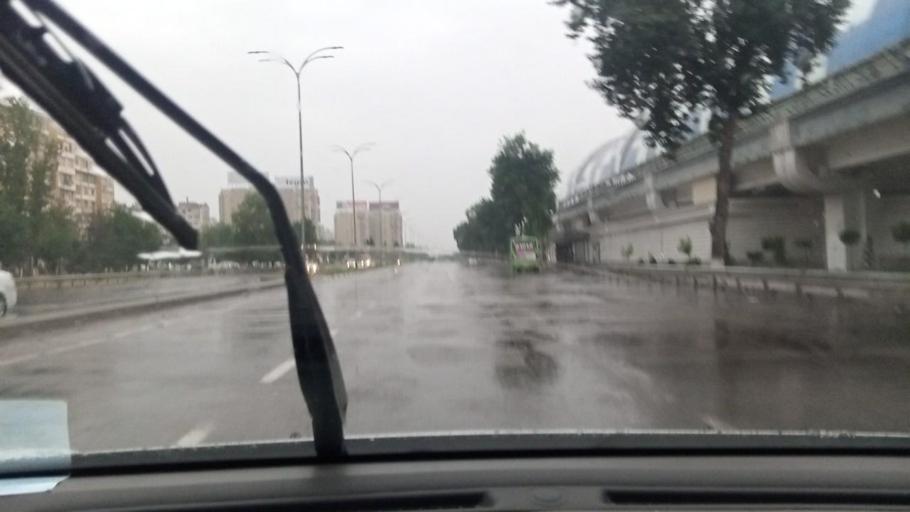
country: UZ
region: Toshkent
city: Salor
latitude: 41.2928
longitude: 69.3560
